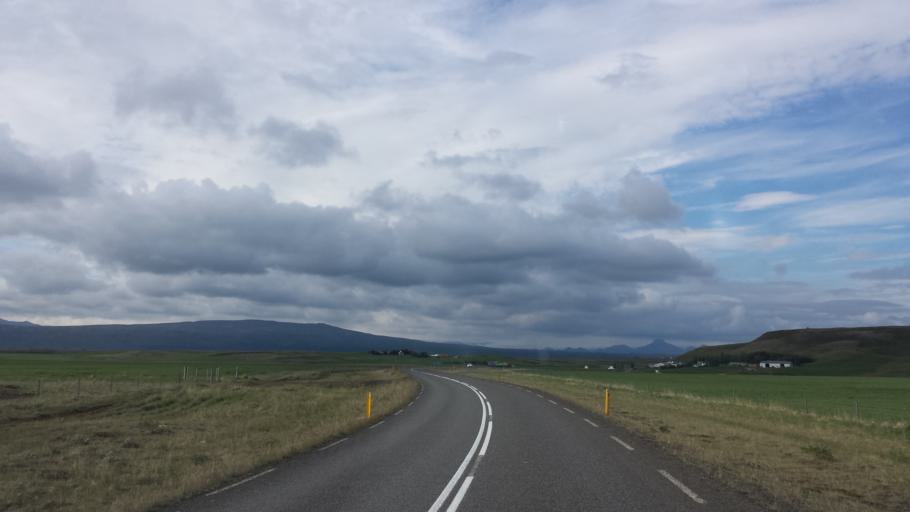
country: IS
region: South
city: Vestmannaeyjar
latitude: 64.2723
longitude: -20.2258
